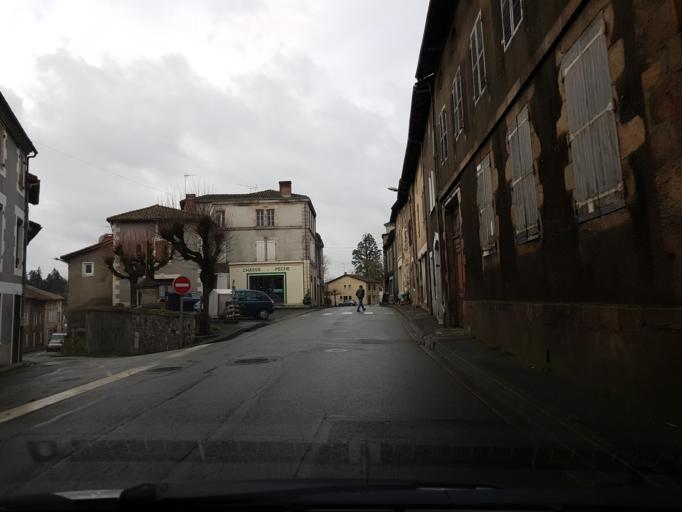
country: FR
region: Poitou-Charentes
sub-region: Departement de la Charente
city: Chabanais
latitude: 45.8767
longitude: 0.7209
